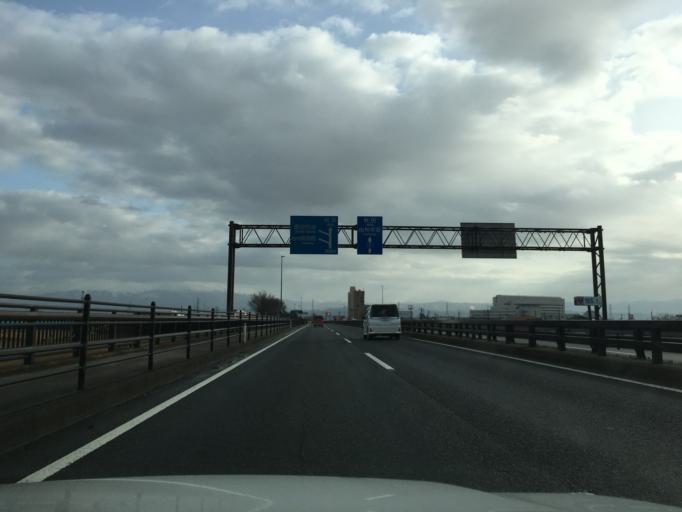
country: JP
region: Yamagata
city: Sakata
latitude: 38.8882
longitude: 139.8450
